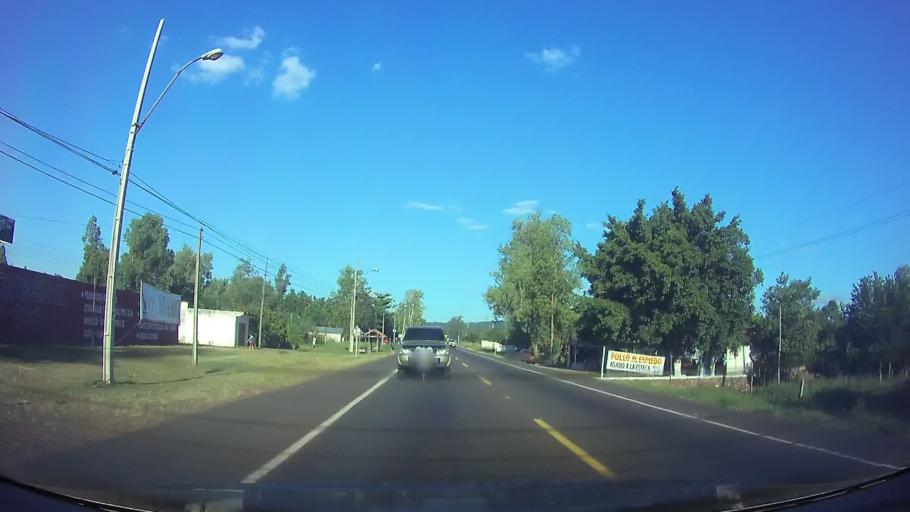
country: PY
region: Central
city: Ypacarai
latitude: -25.3797
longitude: -57.2453
